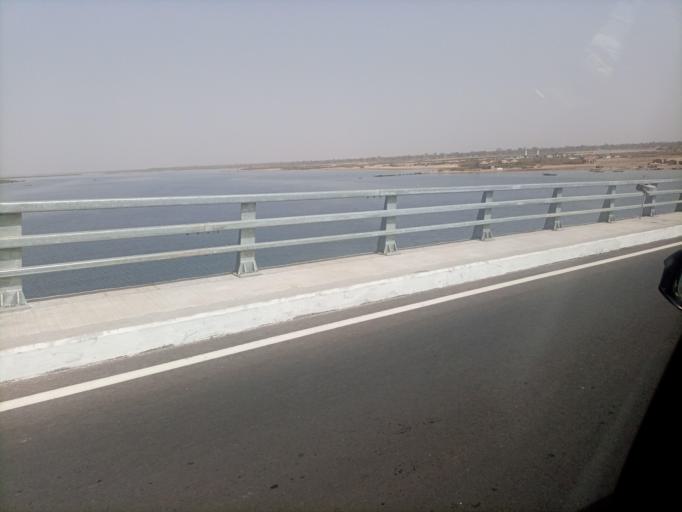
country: SN
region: Fatick
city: Foundiougne
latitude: 14.1334
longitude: -16.4675
